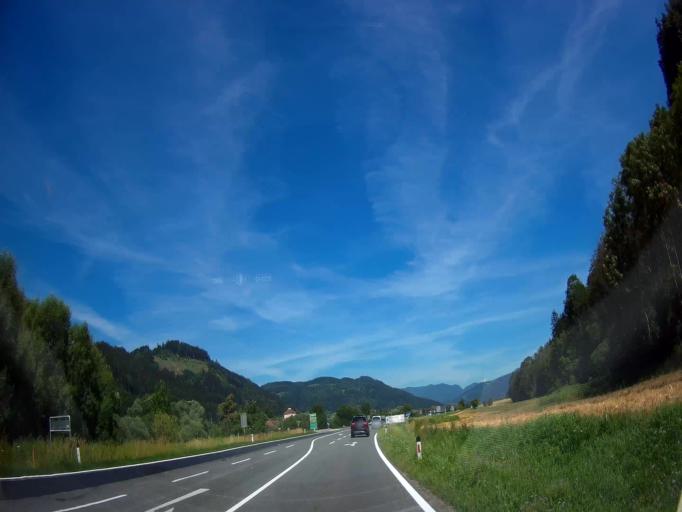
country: AT
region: Carinthia
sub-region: Politischer Bezirk Sankt Veit an der Glan
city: Micheldorf
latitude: 46.9000
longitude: 14.4409
